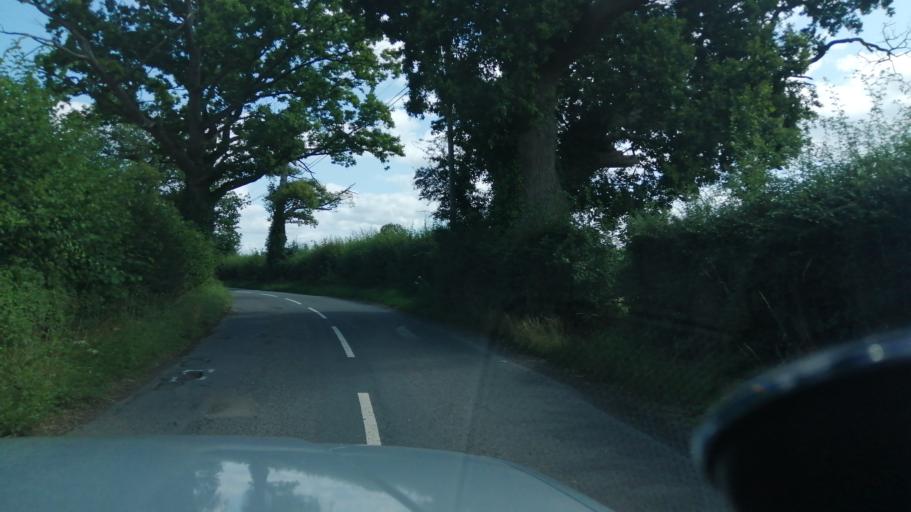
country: GB
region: England
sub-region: Herefordshire
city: Moccas
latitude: 52.0792
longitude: -2.9523
